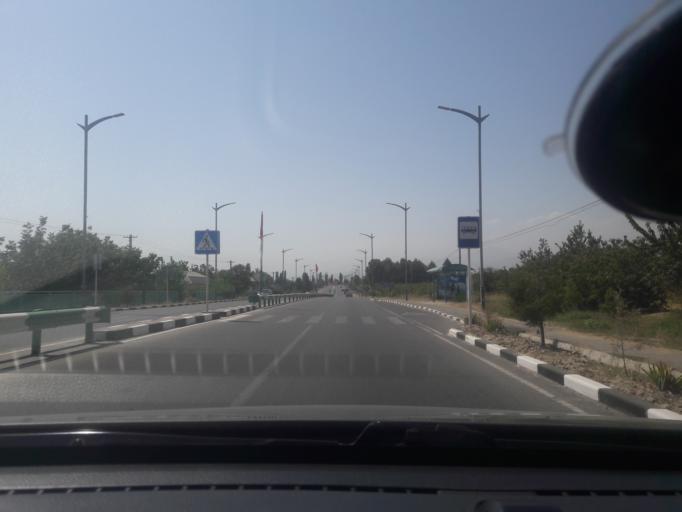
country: TJ
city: Shahrinav
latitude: 38.5641
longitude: 68.4013
